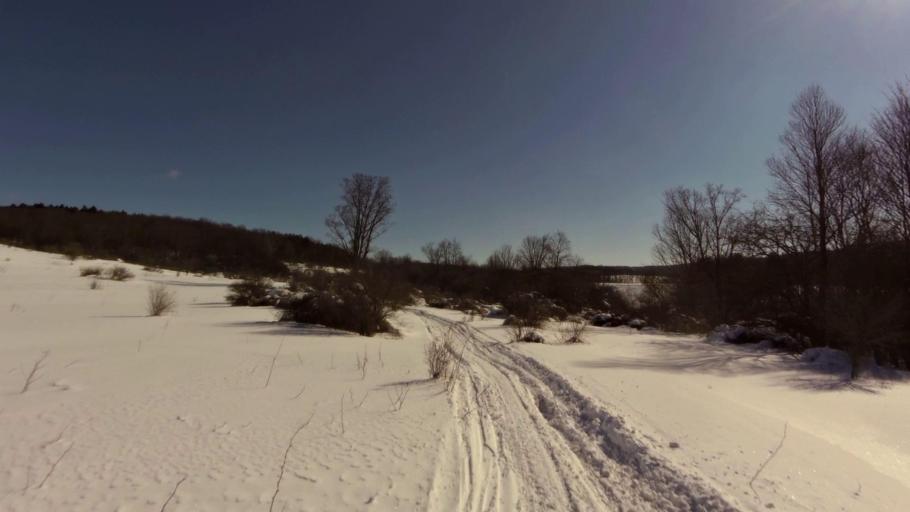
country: US
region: New York
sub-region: Cattaraugus County
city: Franklinville
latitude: 42.3459
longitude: -78.4391
